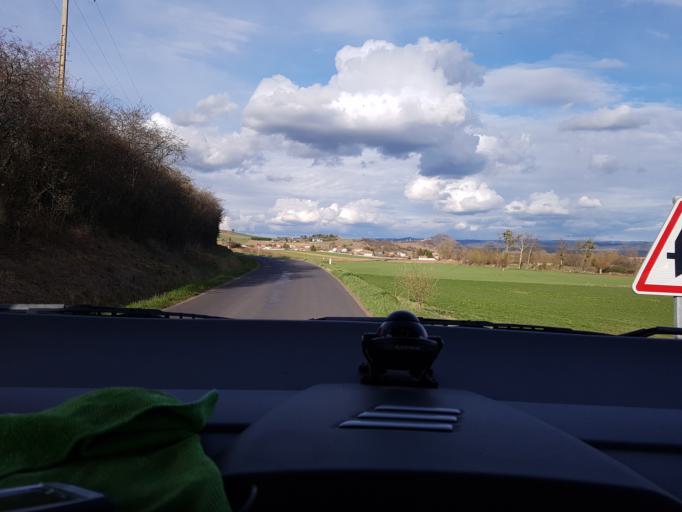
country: FR
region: Auvergne
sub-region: Departement du Puy-de-Dome
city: Saint-Germain-Lembron
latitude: 45.4611
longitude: 3.2248
